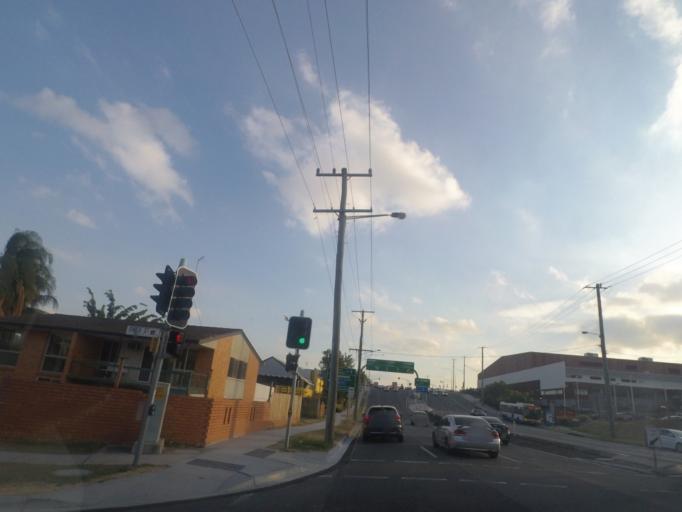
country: AU
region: Queensland
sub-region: Brisbane
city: Nathan
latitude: -27.5586
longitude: 153.0667
